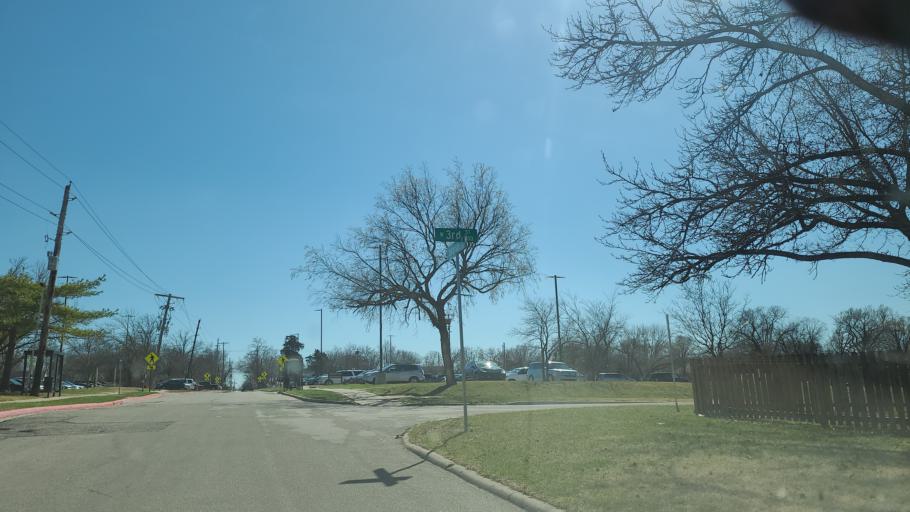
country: US
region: Kansas
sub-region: Douglas County
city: Lawrence
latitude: 38.9791
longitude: -95.2500
